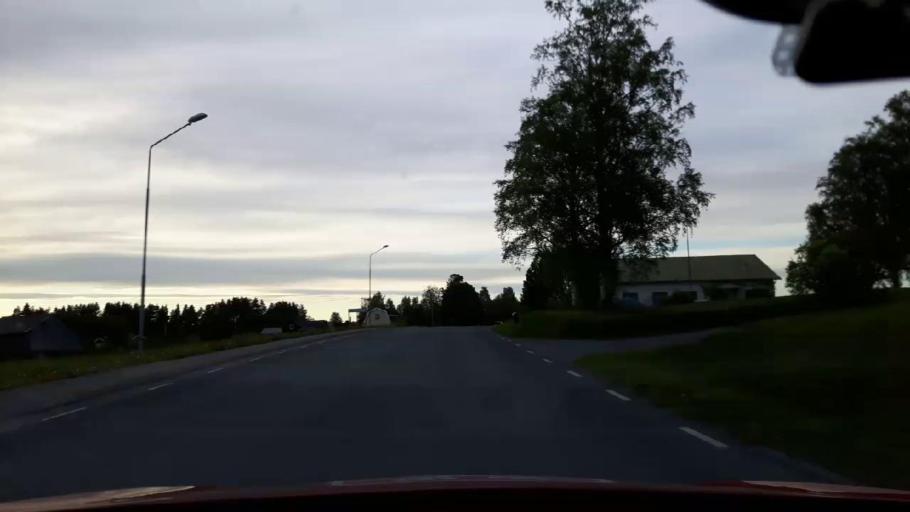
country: SE
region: Jaemtland
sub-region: OEstersunds Kommun
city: Ostersund
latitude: 62.9866
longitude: 14.5785
